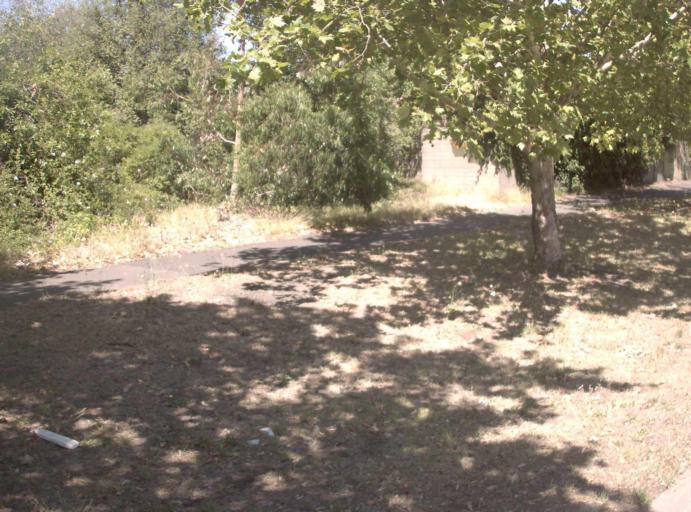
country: AU
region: Victoria
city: Caulfield North
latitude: -37.8687
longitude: 145.0332
